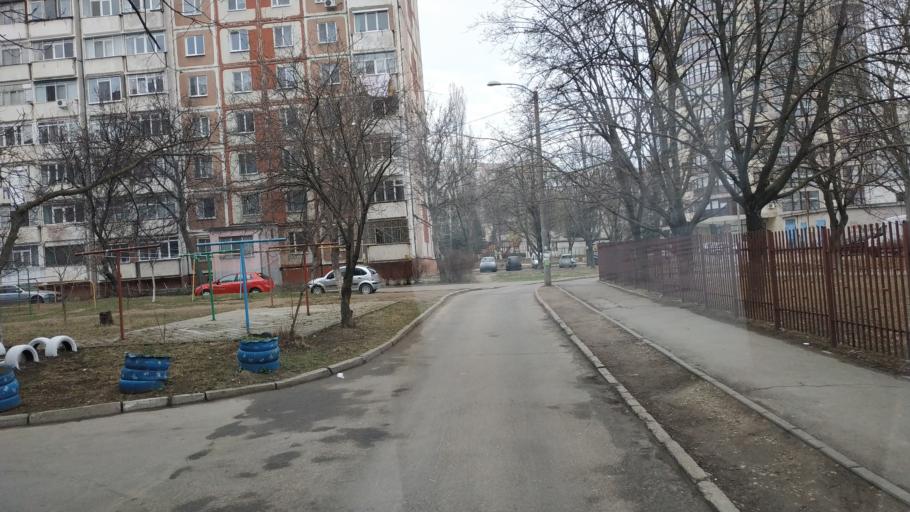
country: MD
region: Chisinau
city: Vatra
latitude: 47.0388
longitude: 28.7727
